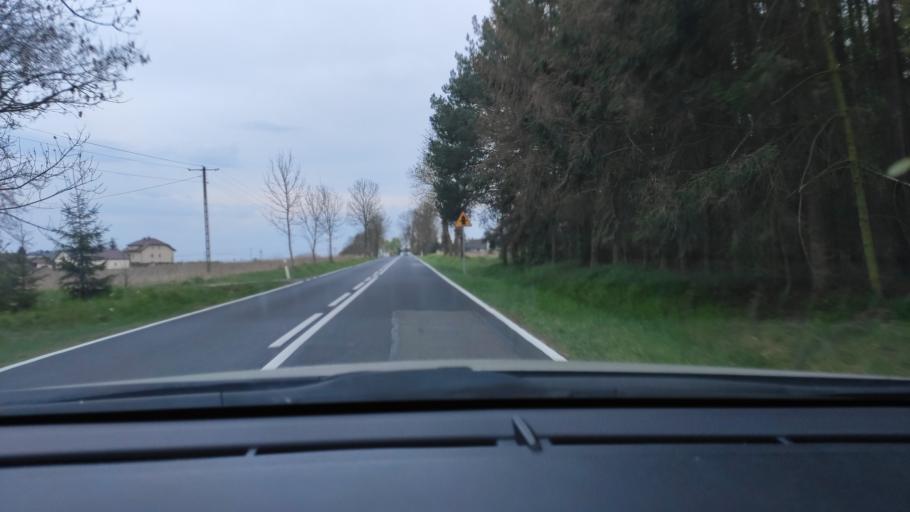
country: PL
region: Masovian Voivodeship
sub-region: Powiat zwolenski
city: Zwolen
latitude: 51.3852
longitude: 21.5552
